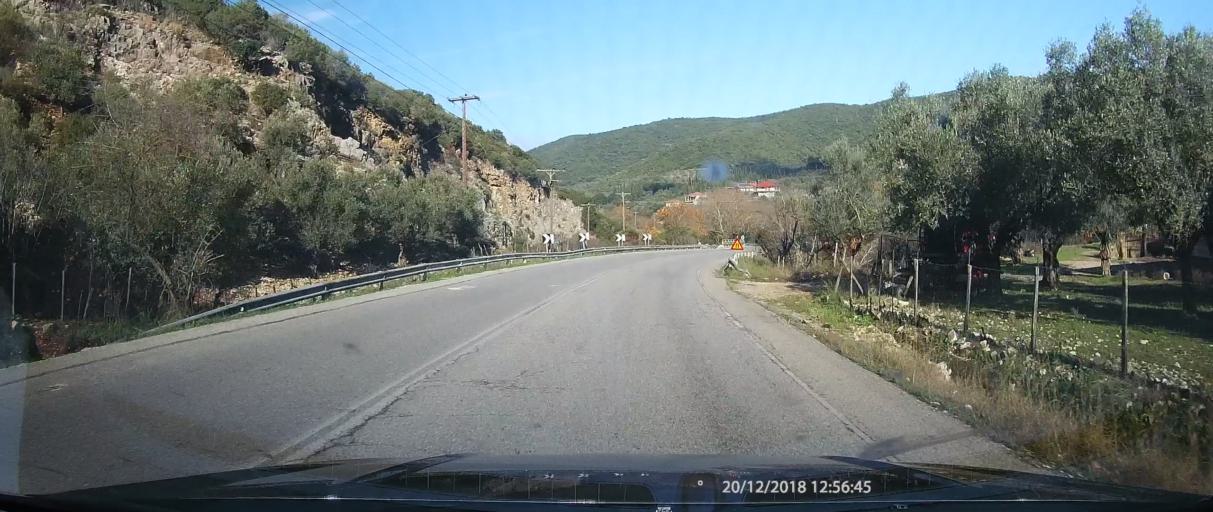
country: GR
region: West Greece
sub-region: Nomos Aitolias kai Akarnanias
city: Pappadhatai
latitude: 38.5145
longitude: 21.3797
